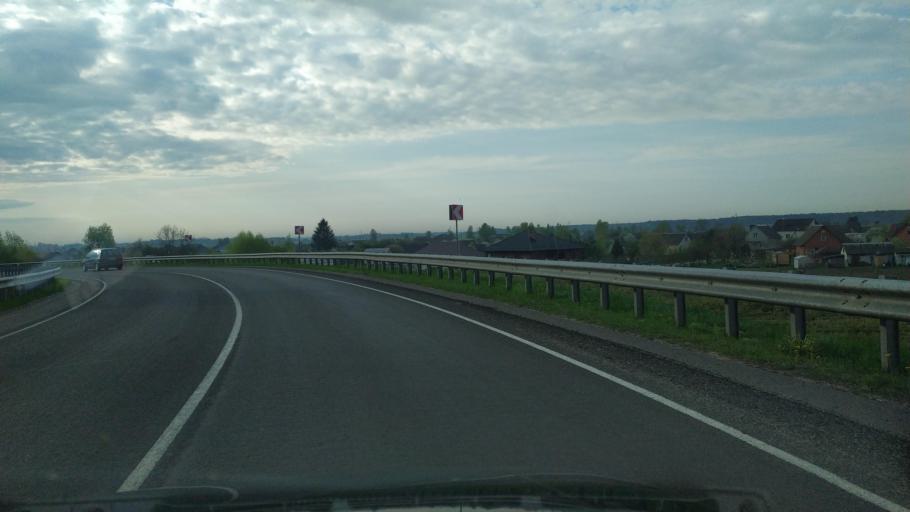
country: BY
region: Brest
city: Zhabinka
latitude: 52.1556
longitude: 24.0555
